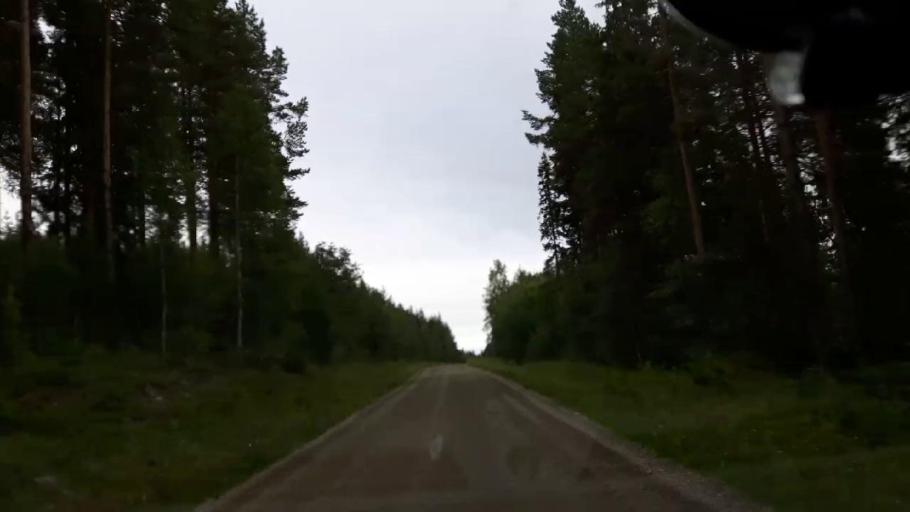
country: SE
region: Jaemtland
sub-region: Braecke Kommun
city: Braecke
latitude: 62.9308
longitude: 15.4866
